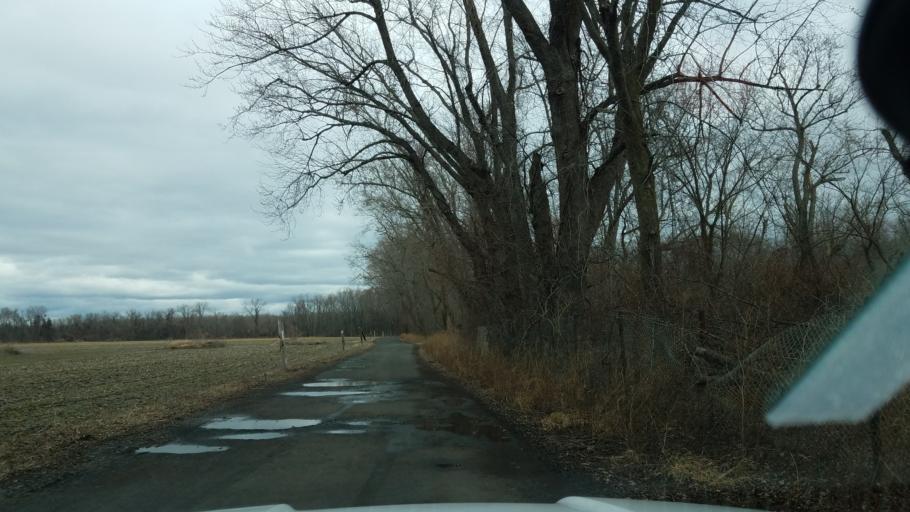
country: US
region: Connecticut
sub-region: Hartford County
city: Wethersfield
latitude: 41.7006
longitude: -72.6365
